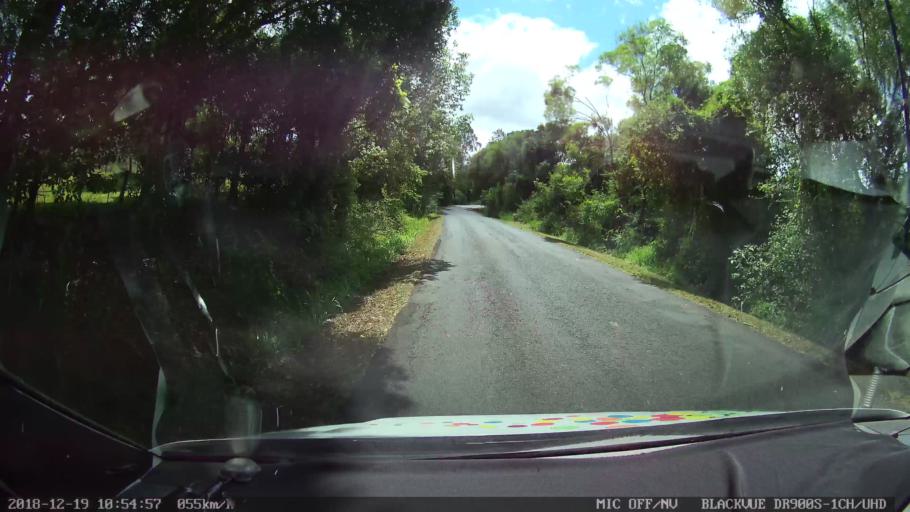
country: AU
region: New South Wales
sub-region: Lismore Municipality
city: Nimbin
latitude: -28.5939
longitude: 153.2501
